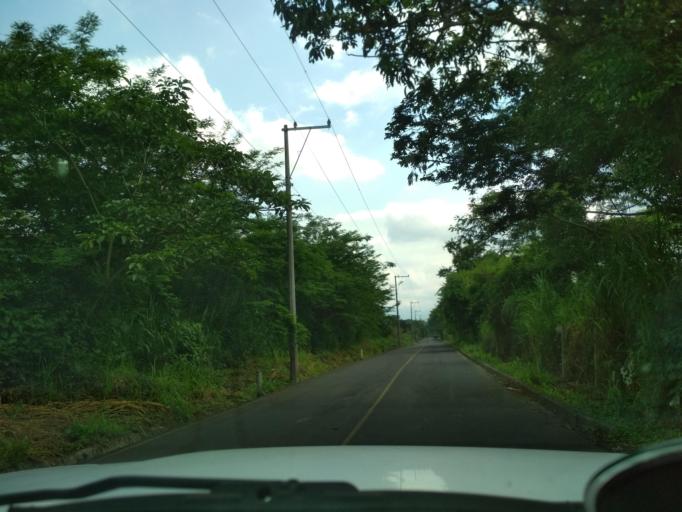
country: MX
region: Veracruz
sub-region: Ixtaczoquitlan
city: Buenavista
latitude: 18.9116
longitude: -97.0269
